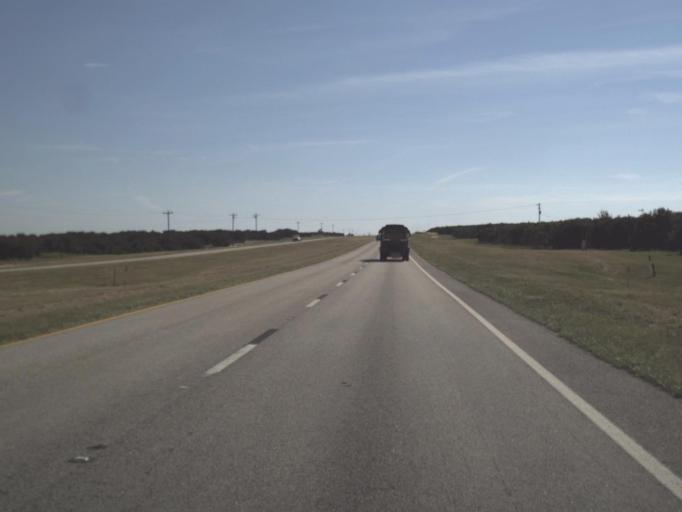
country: US
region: Florida
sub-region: Highlands County
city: Placid Lakes
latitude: 27.1895
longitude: -81.3288
